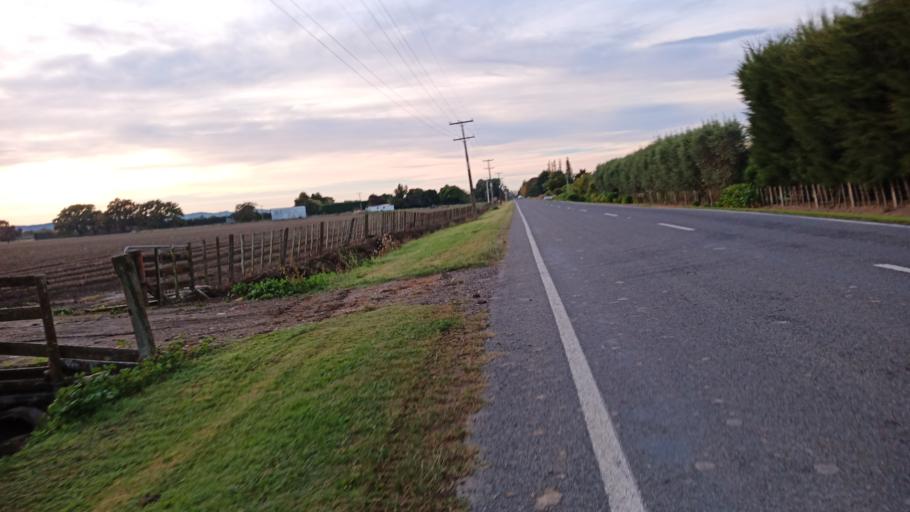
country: NZ
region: Gisborne
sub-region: Gisborne District
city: Gisborne
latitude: -38.6425
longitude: 177.9382
